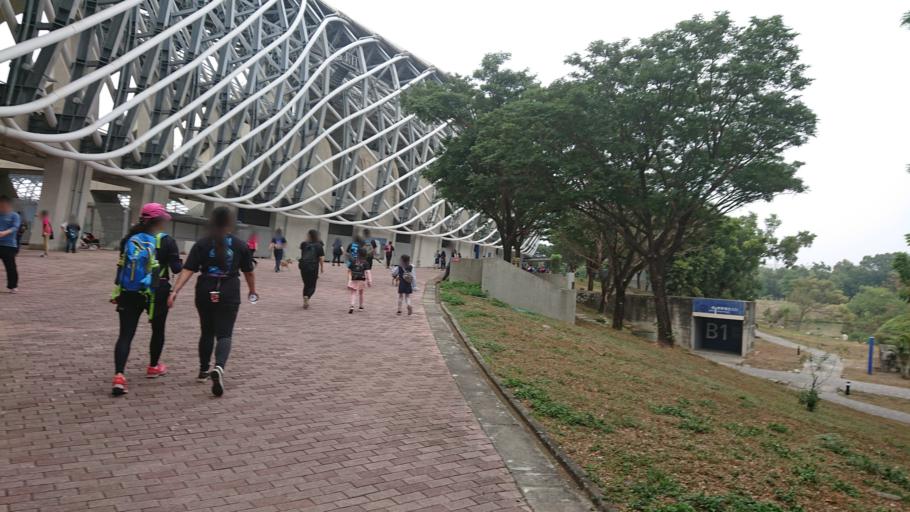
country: TW
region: Kaohsiung
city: Kaohsiung
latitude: 22.7021
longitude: 120.2958
